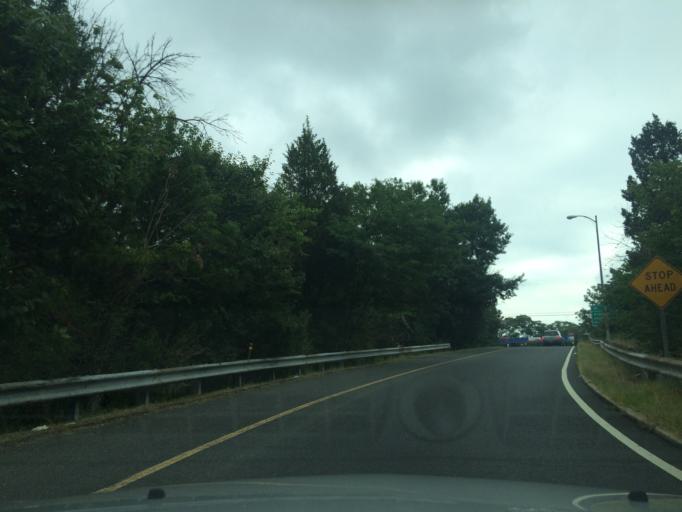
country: US
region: Maryland
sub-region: Prince George's County
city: Morningside
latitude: 38.8278
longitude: -76.8800
